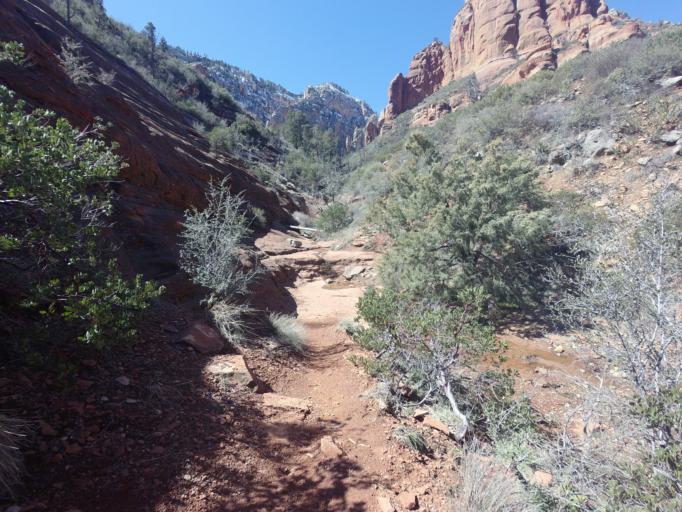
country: US
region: Arizona
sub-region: Coconino County
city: Sedona
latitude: 34.9361
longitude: -111.7482
